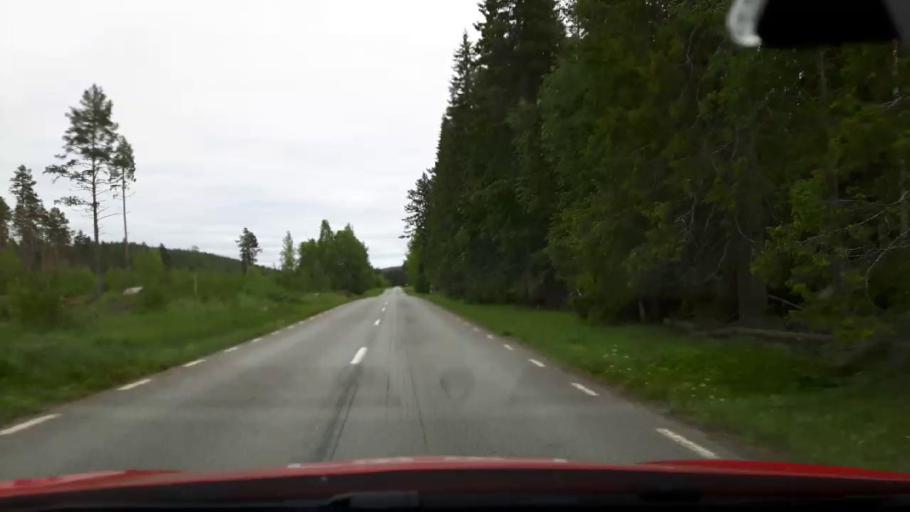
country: SE
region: Jaemtland
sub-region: Stroemsunds Kommun
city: Stroemsund
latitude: 63.4410
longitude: 15.4831
